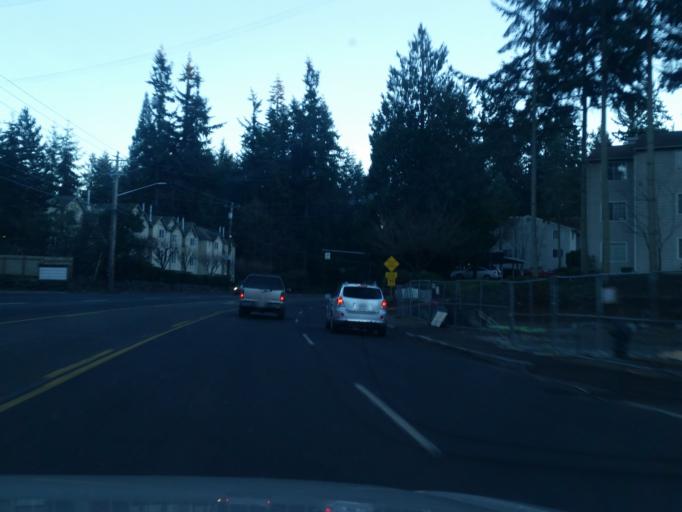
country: US
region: Washington
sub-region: Snohomish County
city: Esperance
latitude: 47.7883
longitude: -122.3545
